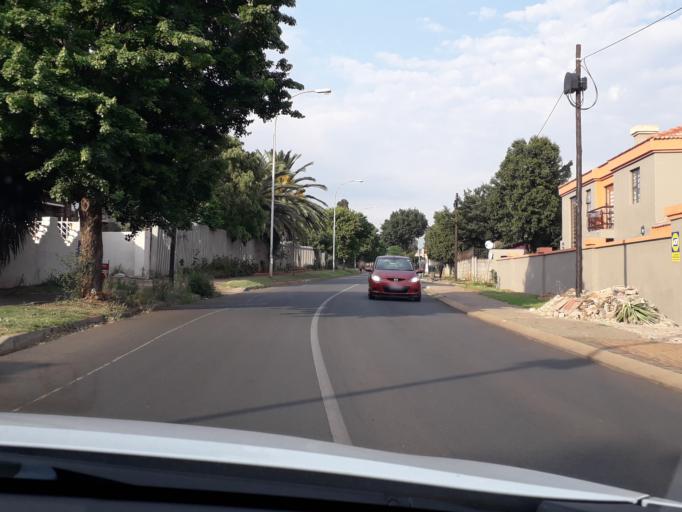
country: ZA
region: Gauteng
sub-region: City of Johannesburg Metropolitan Municipality
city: Johannesburg
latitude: -26.1644
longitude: 27.9806
